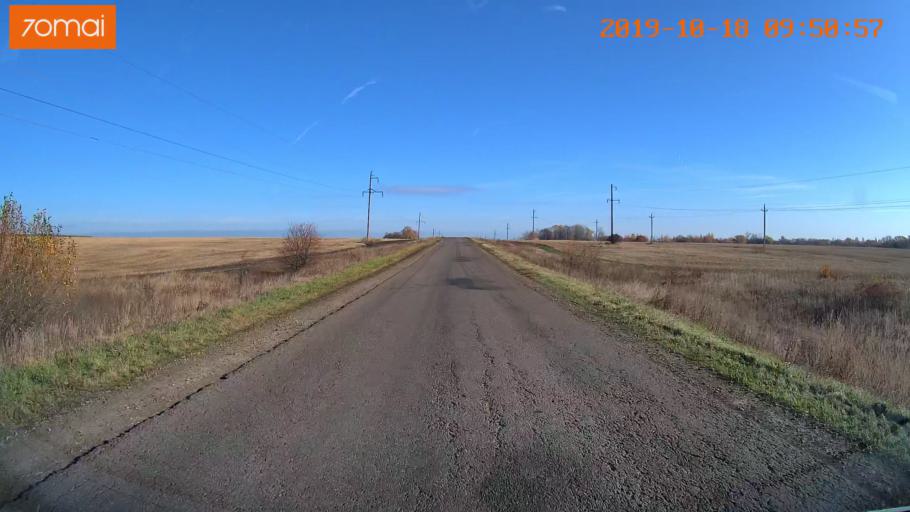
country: RU
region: Tula
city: Kazachka
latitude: 53.3349
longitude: 38.2856
